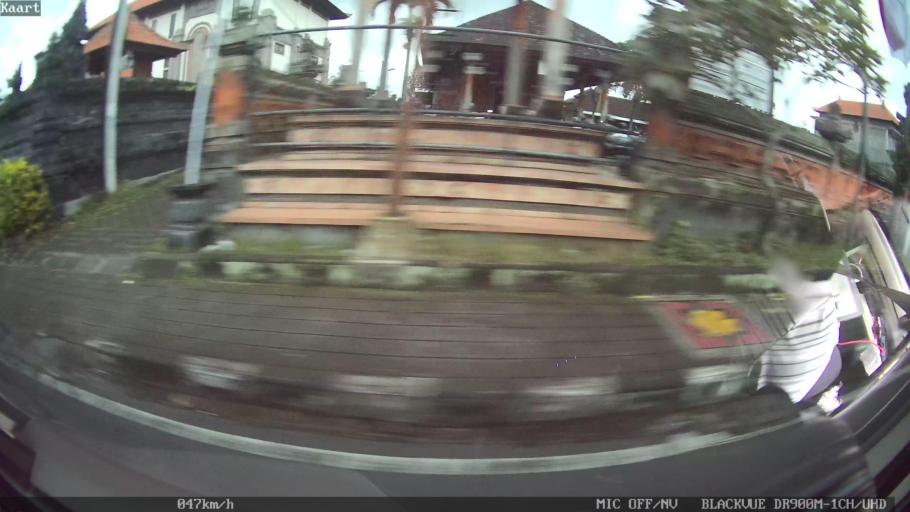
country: ID
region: Bali
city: Petang
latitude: -8.4007
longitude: 115.2185
